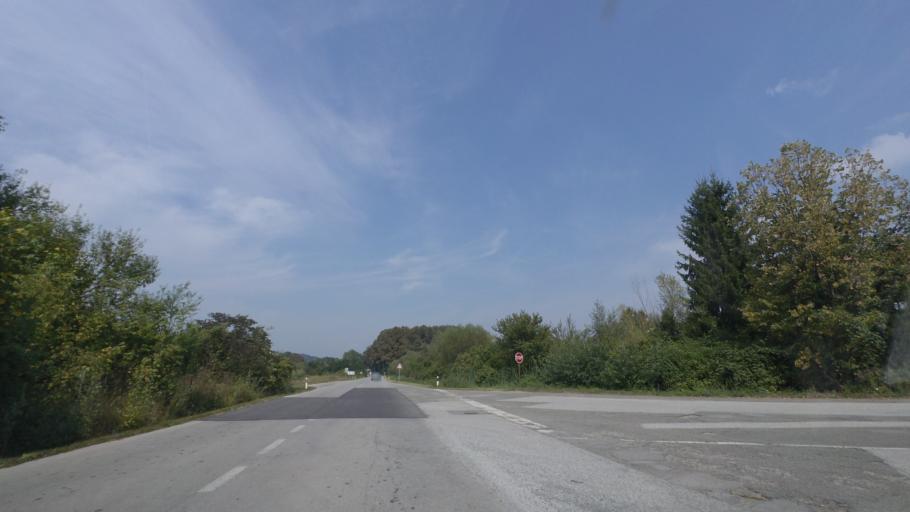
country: HR
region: Sisacko-Moslavacka
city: Glina
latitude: 45.2998
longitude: 16.1316
